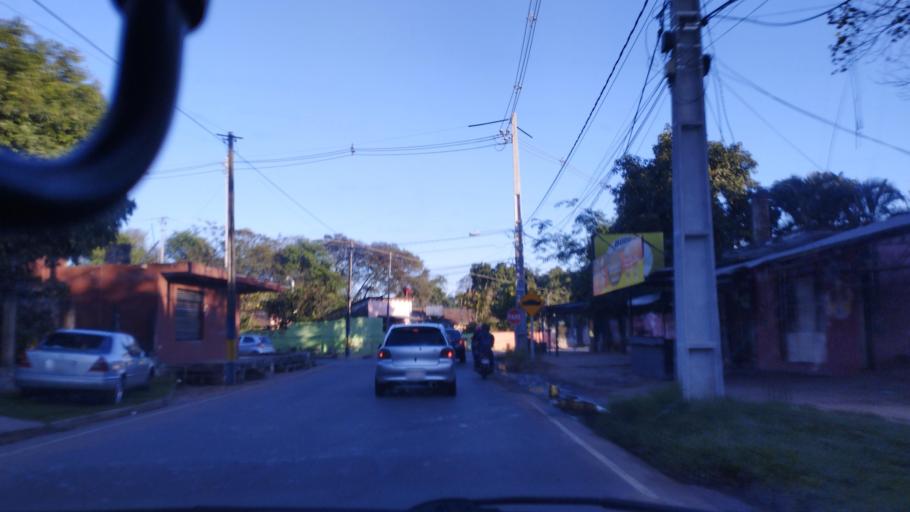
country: PY
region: Central
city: Fernando de la Mora
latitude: -25.2829
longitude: -57.5188
